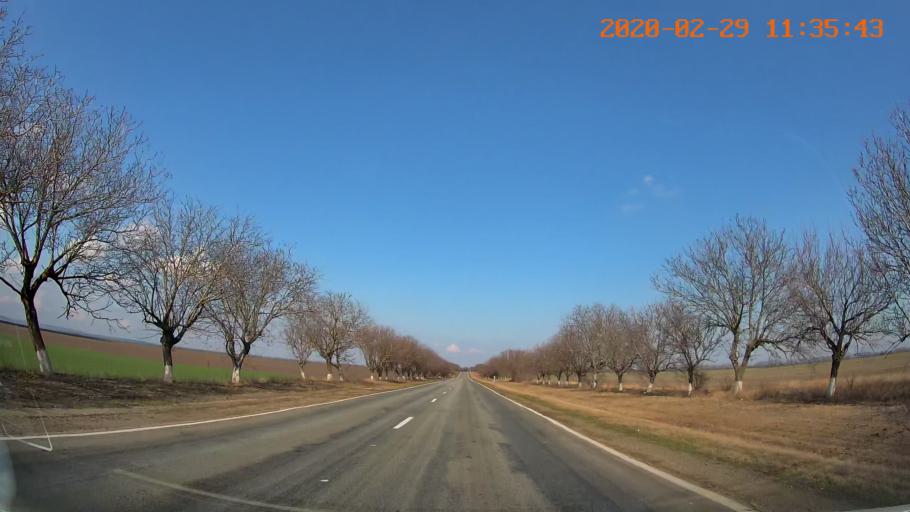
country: MD
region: Rezina
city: Saharna
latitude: 47.5847
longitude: 29.0615
